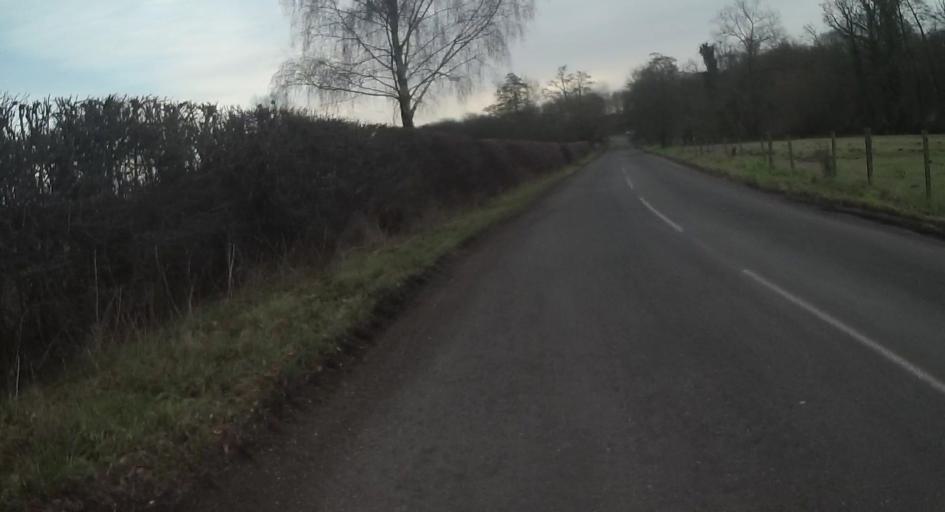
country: GB
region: England
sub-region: Hampshire
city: Highclere
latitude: 51.2245
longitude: -1.3781
